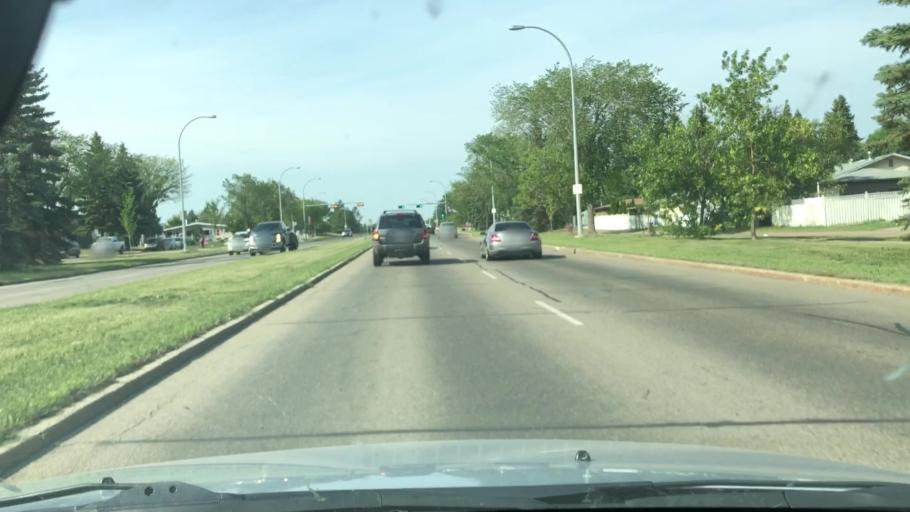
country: CA
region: Alberta
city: Edmonton
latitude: 53.6082
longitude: -113.4428
